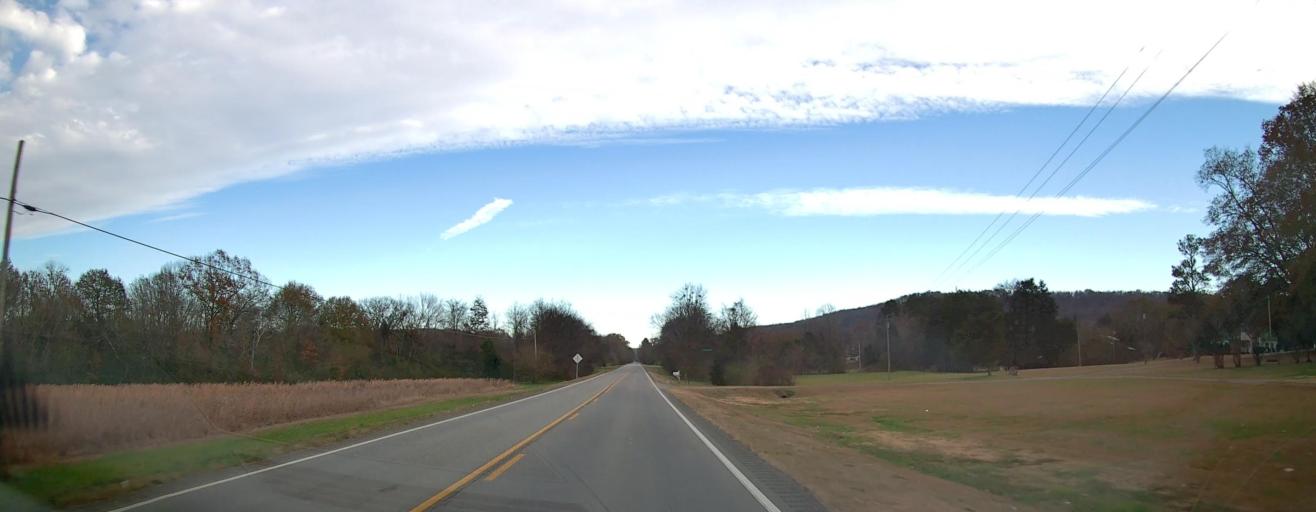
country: US
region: Alabama
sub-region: Marshall County
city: Arab
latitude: 34.3981
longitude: -86.6798
